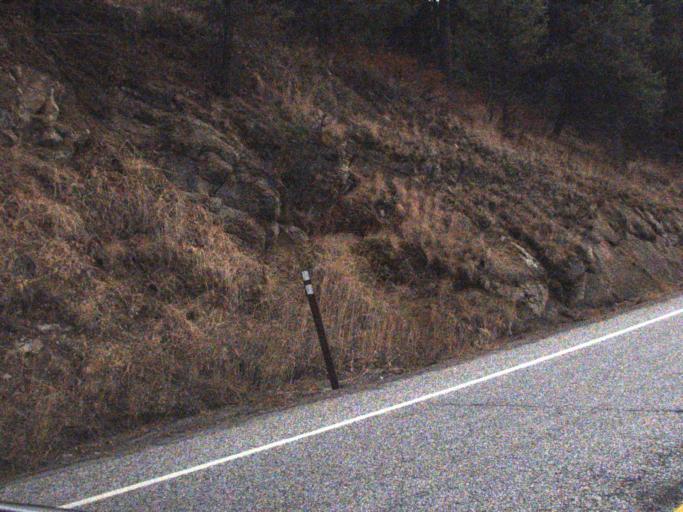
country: US
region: Washington
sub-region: Ferry County
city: Republic
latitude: 48.6139
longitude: -118.5720
